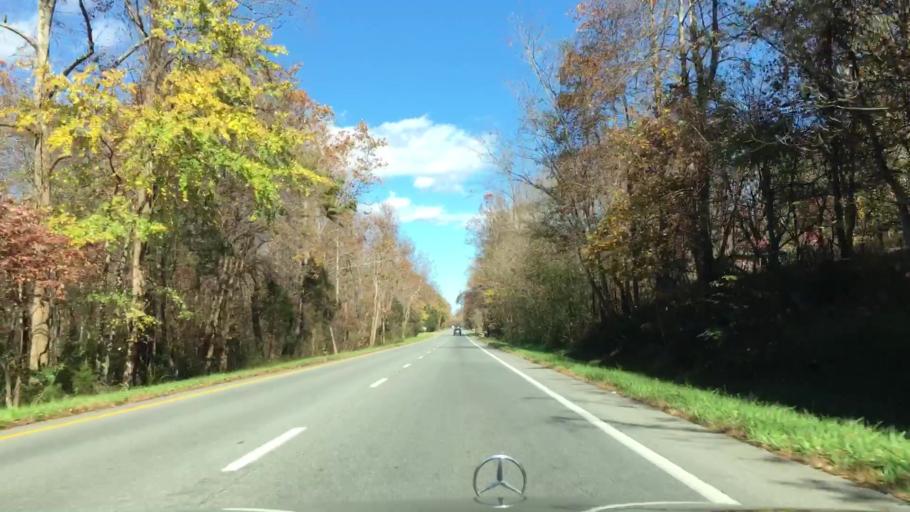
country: US
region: Virginia
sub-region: Albemarle County
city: Crozet
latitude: 37.9350
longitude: -78.6716
